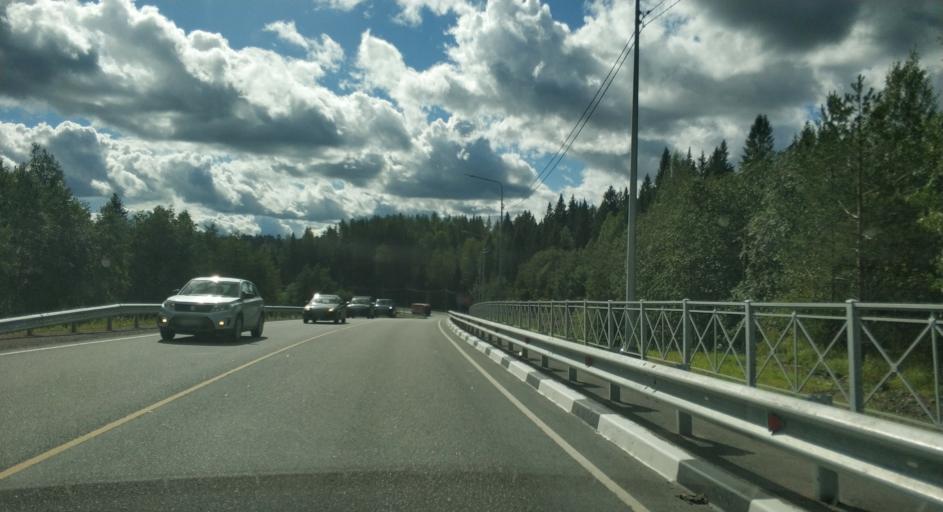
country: RU
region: Republic of Karelia
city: Ruskeala
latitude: 61.9430
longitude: 30.5939
